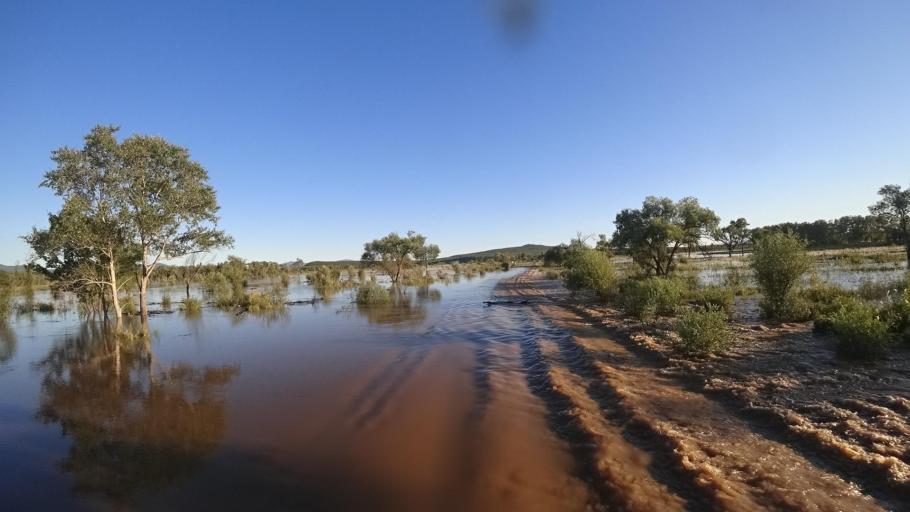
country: RU
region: Primorskiy
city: Kirovskiy
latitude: 44.7780
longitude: 133.6263
